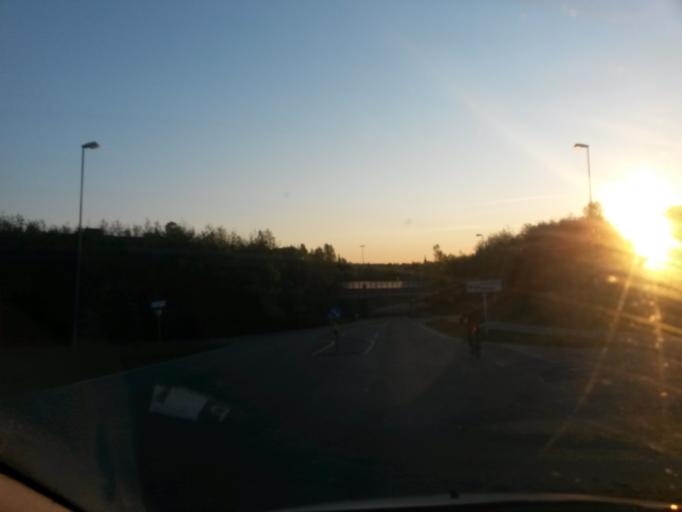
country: NO
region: Akershus
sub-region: Asker
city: Asker
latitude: 59.8314
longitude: 10.4185
